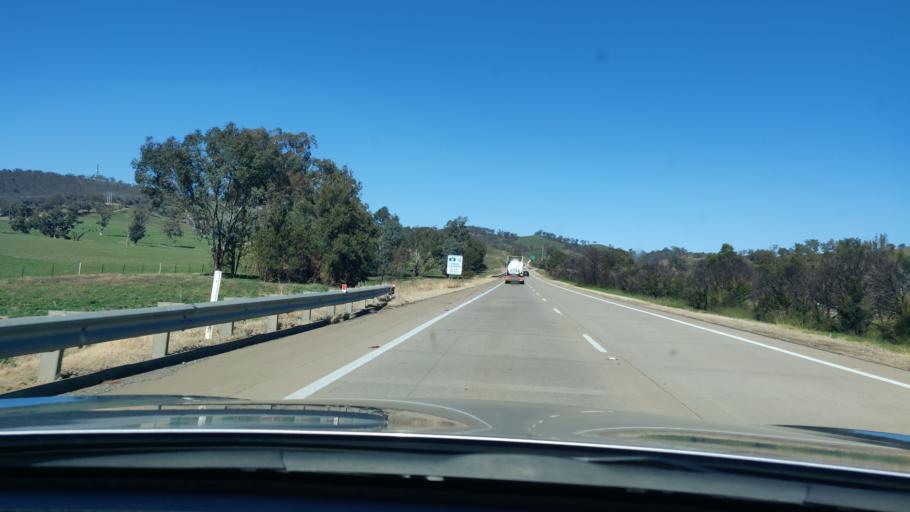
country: AU
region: New South Wales
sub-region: Gundagai
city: Gundagai
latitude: -35.1972
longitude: 147.8175
